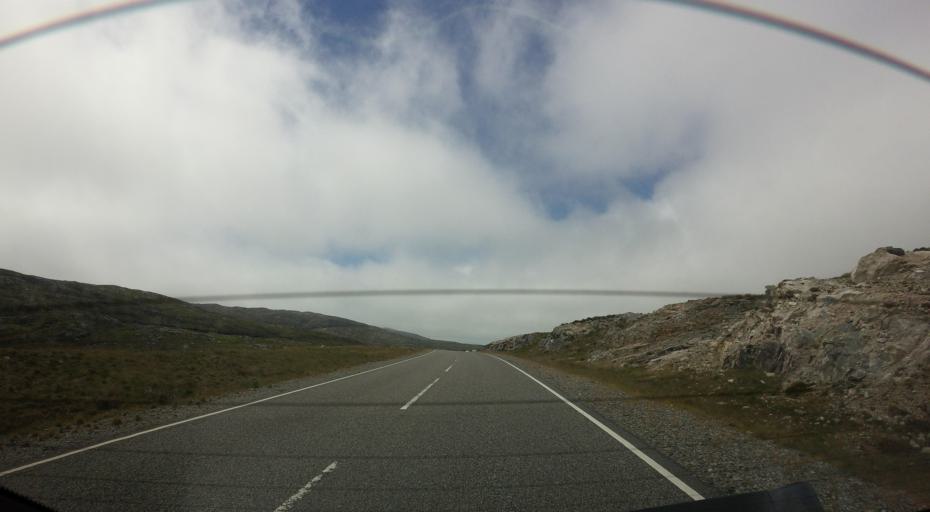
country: GB
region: Scotland
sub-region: Eilean Siar
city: Harris
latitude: 57.8564
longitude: -6.8530
